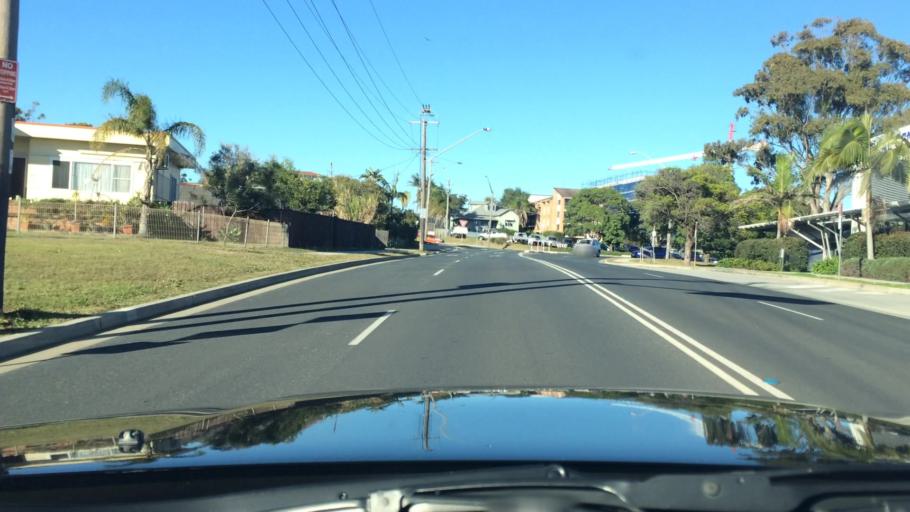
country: AU
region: New South Wales
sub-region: Port Macquarie-Hastings
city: Port Macquarie
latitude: -31.4324
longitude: 152.8994
